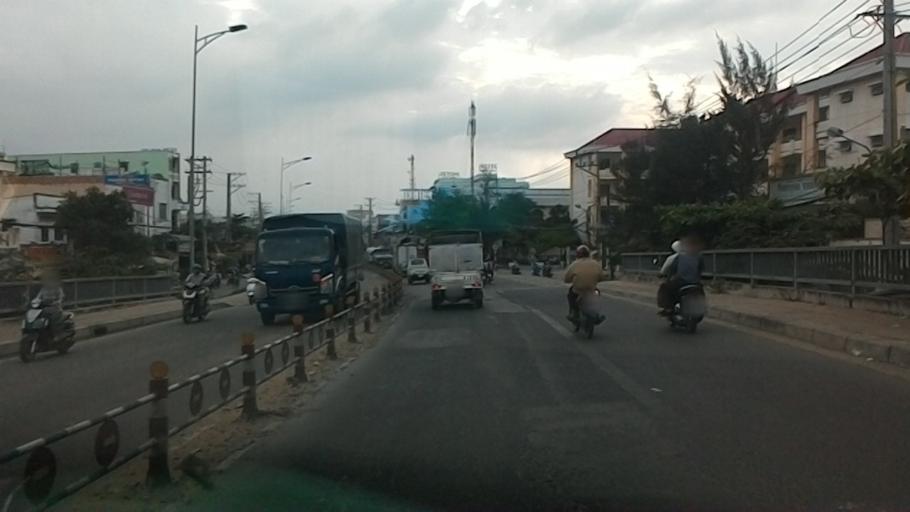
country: VN
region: Can Tho
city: Cai Rang
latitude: 10.0122
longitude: 105.7533
